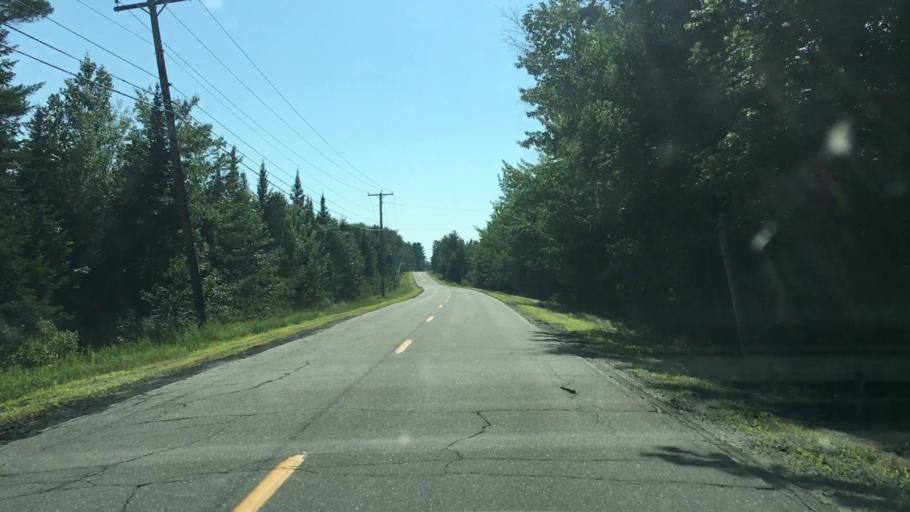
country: US
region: Maine
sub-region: Penobscot County
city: Enfield
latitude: 45.2445
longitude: -68.6114
